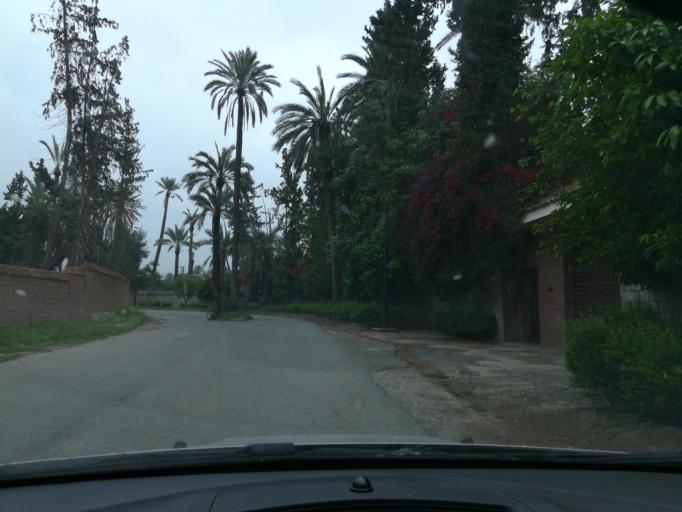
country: MA
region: Marrakech-Tensift-Al Haouz
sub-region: Marrakech
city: Marrakesh
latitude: 31.6523
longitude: -7.9780
